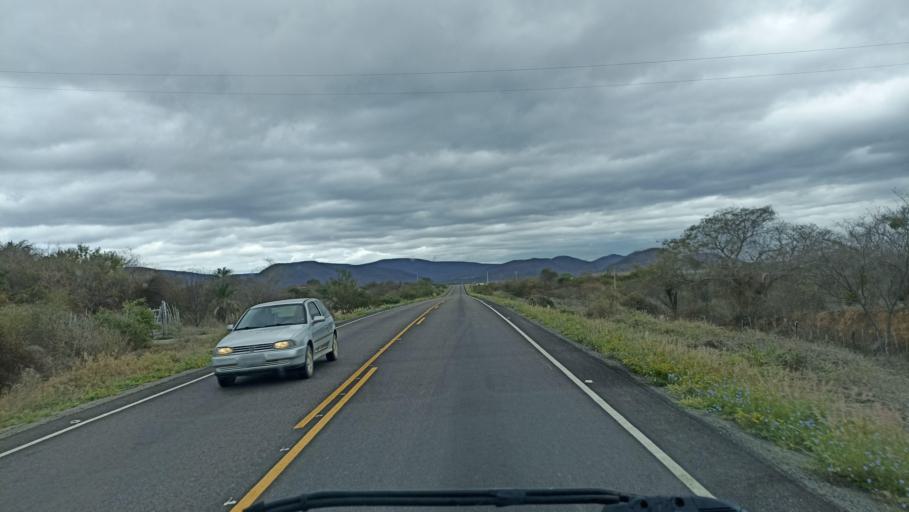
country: BR
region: Bahia
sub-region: Iacu
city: Iacu
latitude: -12.9118
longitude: -40.4091
